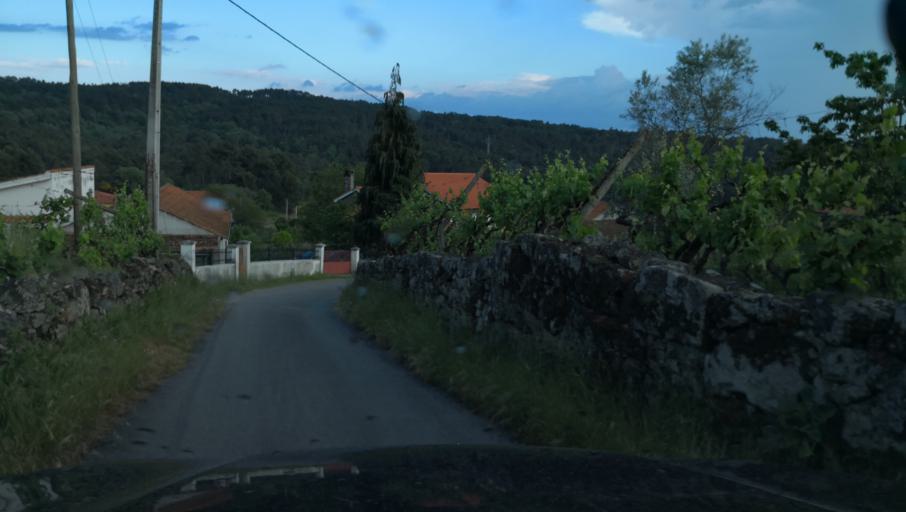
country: PT
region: Vila Real
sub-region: Vila Real
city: Vila Real
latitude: 41.3158
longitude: -7.6821
